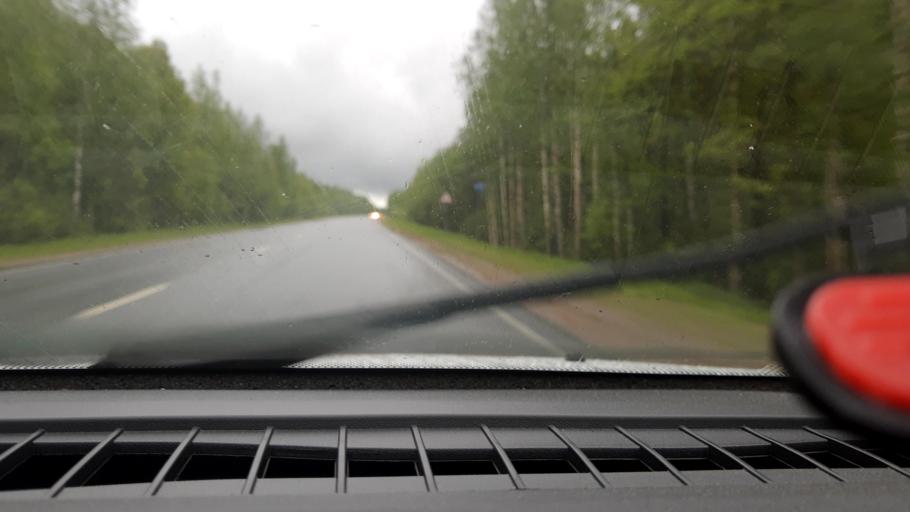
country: RU
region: Nizjnij Novgorod
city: Semenov
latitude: 56.7818
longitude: 44.4353
